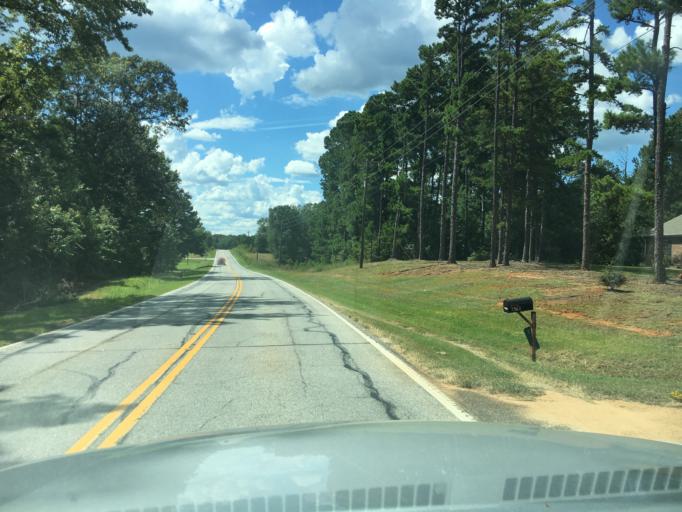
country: US
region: South Carolina
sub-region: Laurens County
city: Laurens
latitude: 34.5178
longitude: -82.1003
